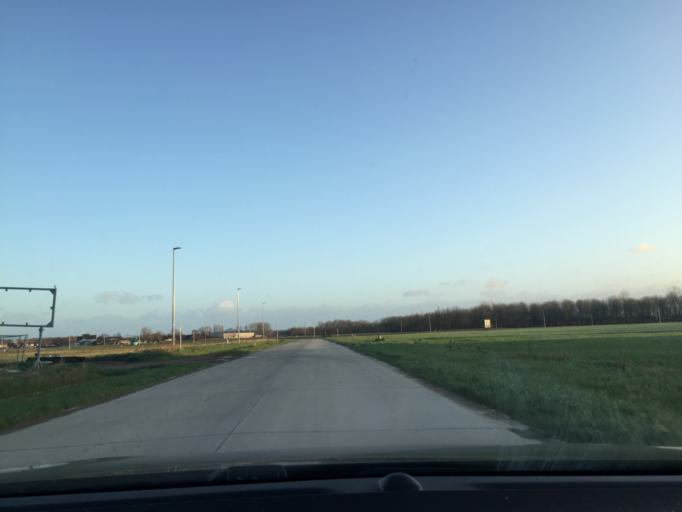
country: BE
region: Flanders
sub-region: Provincie West-Vlaanderen
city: Ardooie
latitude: 50.9753
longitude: 3.1584
